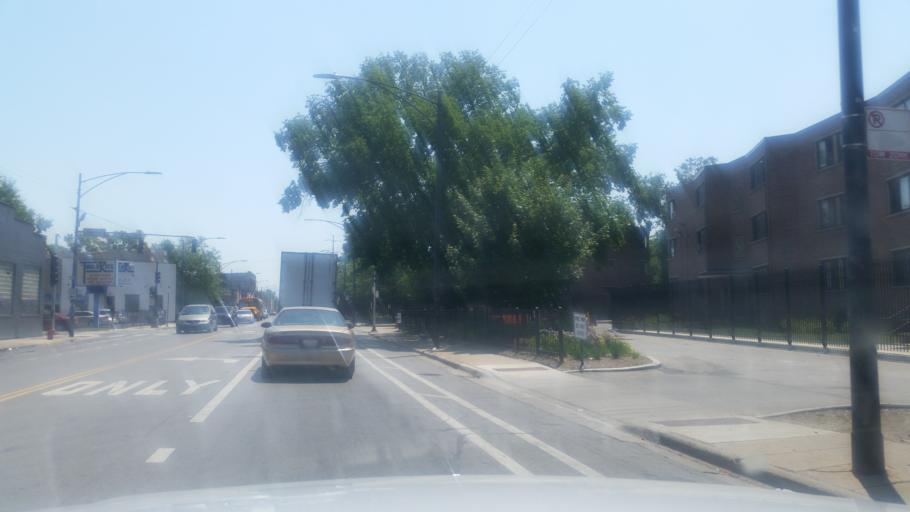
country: US
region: Illinois
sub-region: Cook County
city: Chicago
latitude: 41.7771
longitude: -87.6156
